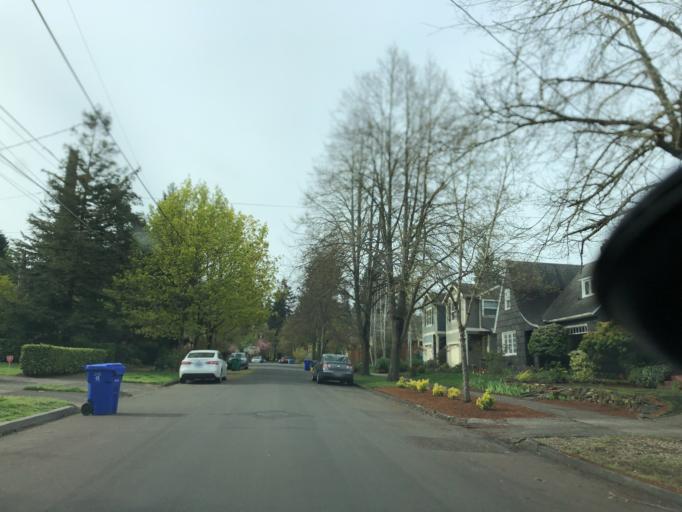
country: US
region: Oregon
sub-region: Multnomah County
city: Portland
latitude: 45.5562
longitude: -122.6276
